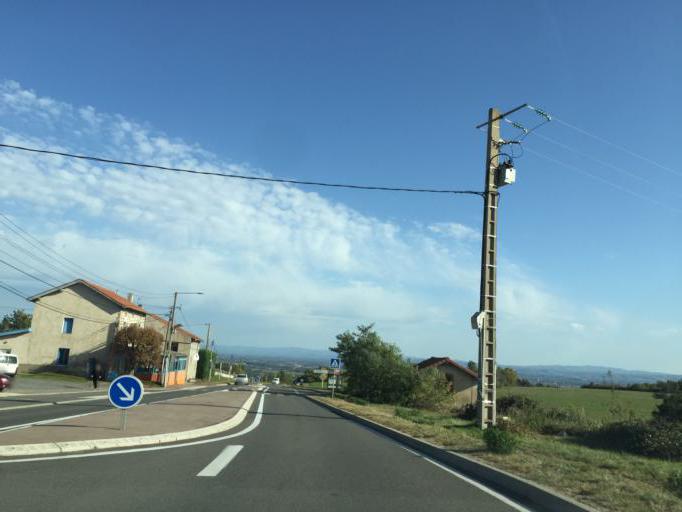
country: FR
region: Rhone-Alpes
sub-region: Departement de la Loire
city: Saint-Marcellin-en-Forez
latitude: 45.4748
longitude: 4.1461
